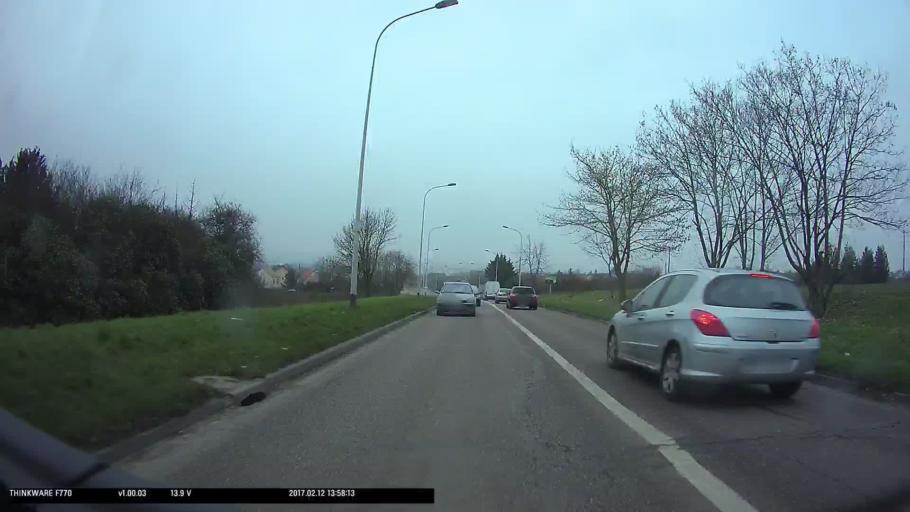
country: FR
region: Ile-de-France
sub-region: Departement des Yvelines
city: Andresy
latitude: 48.9782
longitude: 2.0459
